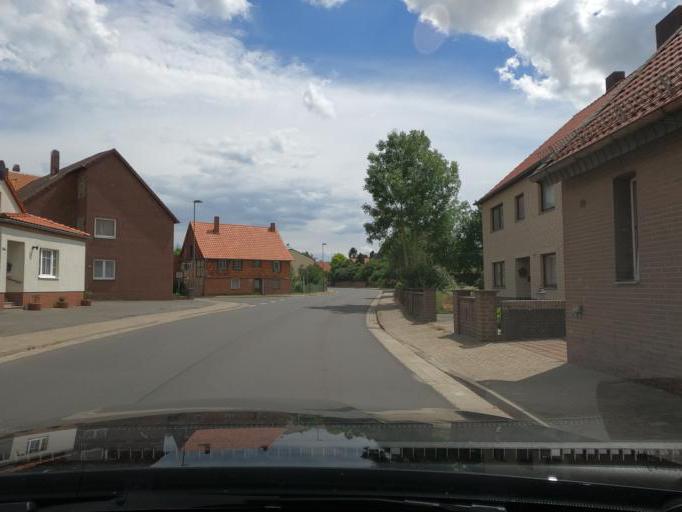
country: DE
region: Lower Saxony
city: Hohenhameln
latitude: 52.2514
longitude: 10.0211
